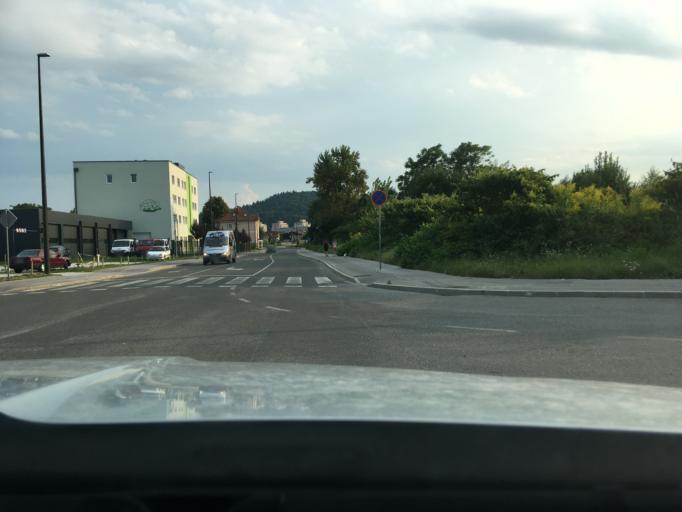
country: SI
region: Ljubljana
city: Ljubljana
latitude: 46.0750
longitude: 14.4956
